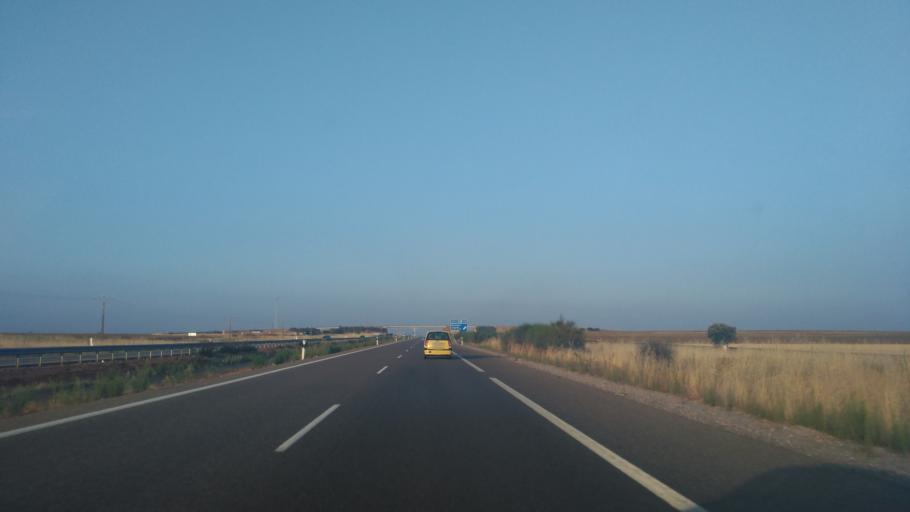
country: ES
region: Castille and Leon
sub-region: Provincia de Salamanca
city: Galindo y Perahuy
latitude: 40.9222
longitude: -5.8428
